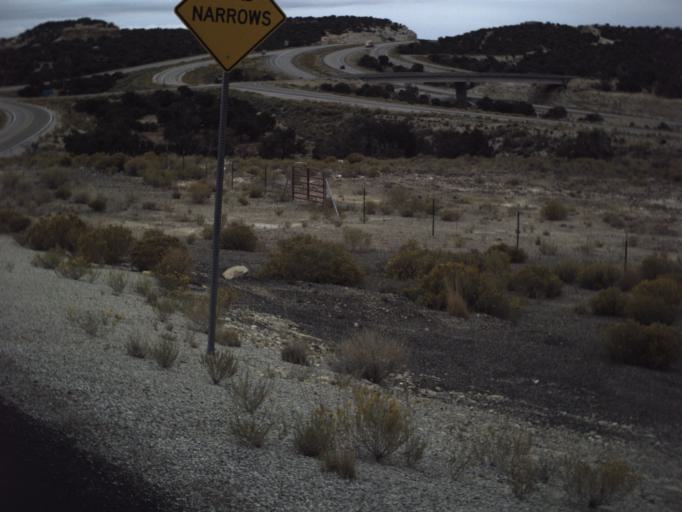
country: US
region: Utah
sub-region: Emery County
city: Ferron
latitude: 38.8581
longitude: -110.9176
